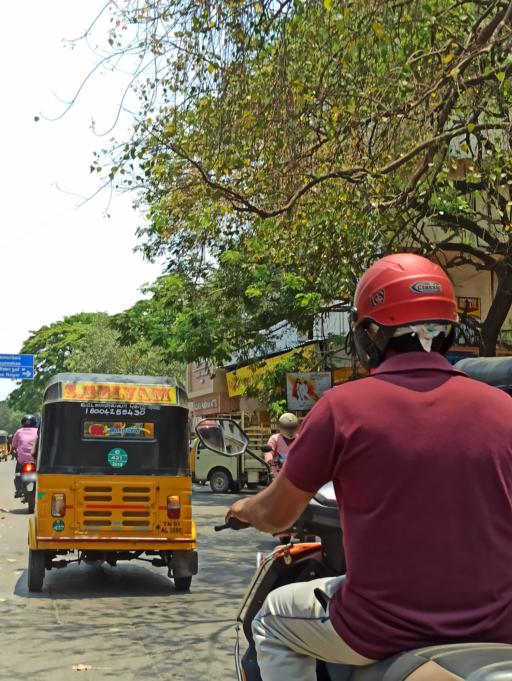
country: IN
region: Tamil Nadu
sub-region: Chennai
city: Chetput
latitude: 13.0846
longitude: 80.2341
